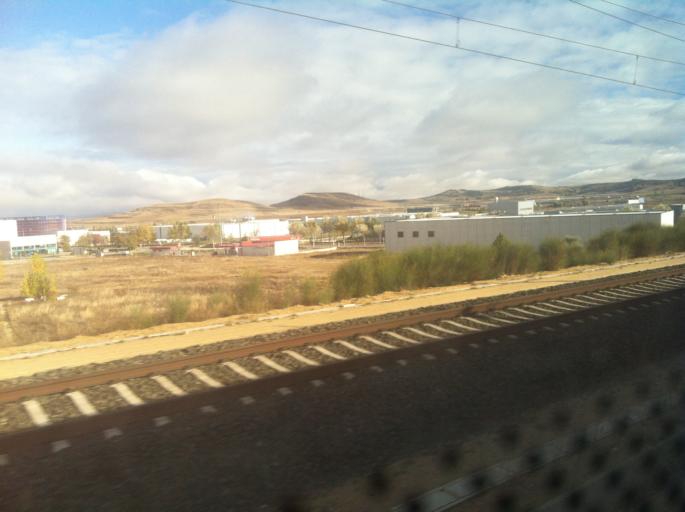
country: ES
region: Castille and Leon
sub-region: Provincia de Burgos
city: Sotragero
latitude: 42.3683
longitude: -3.7196
